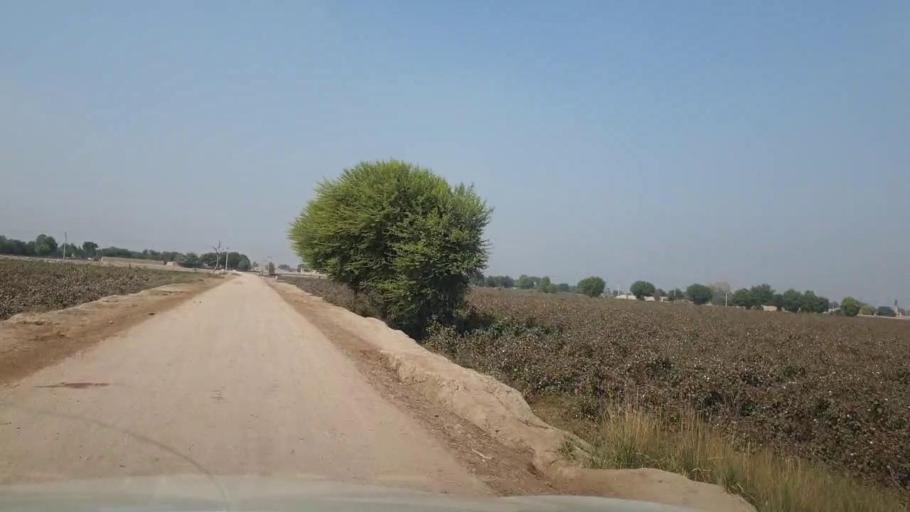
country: PK
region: Sindh
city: Bhan
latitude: 26.5428
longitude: 67.7394
